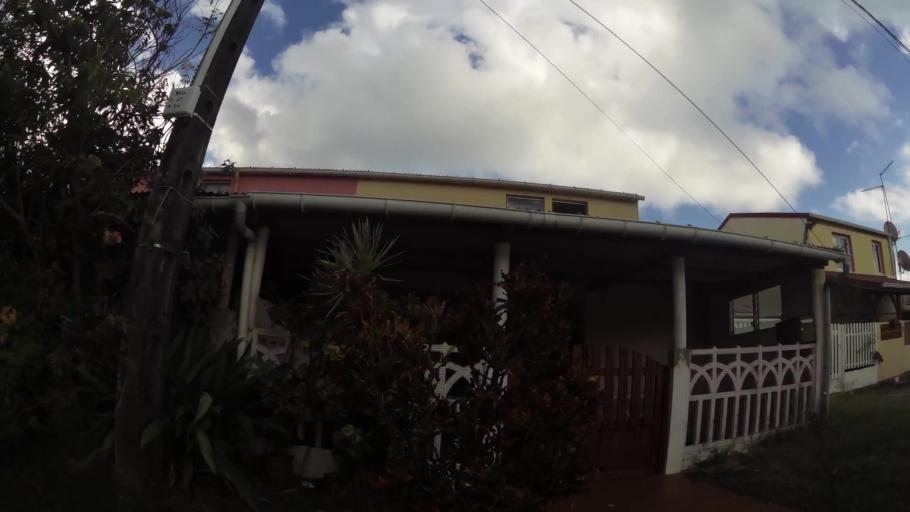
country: MQ
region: Martinique
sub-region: Martinique
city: Le Vauclin
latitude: 14.5458
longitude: -60.8427
